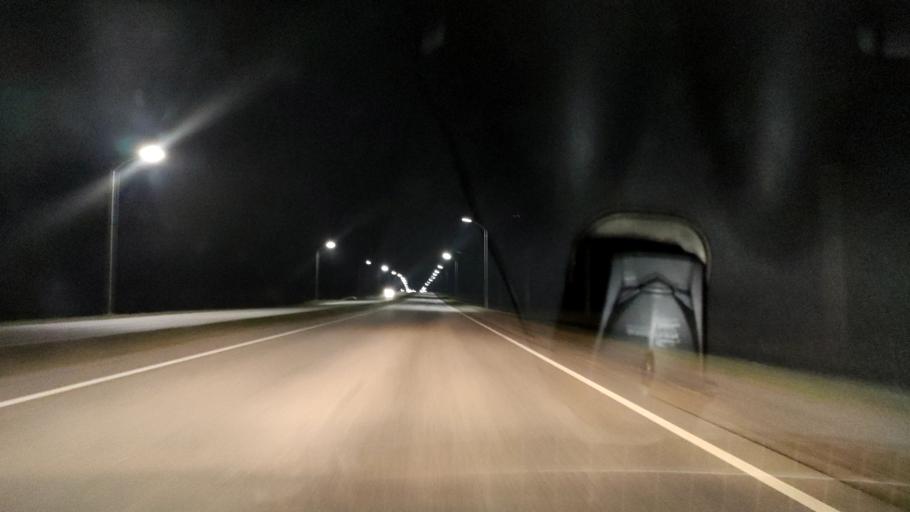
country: RU
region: Belgorod
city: Staryy Oskol
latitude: 51.3826
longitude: 37.8567
